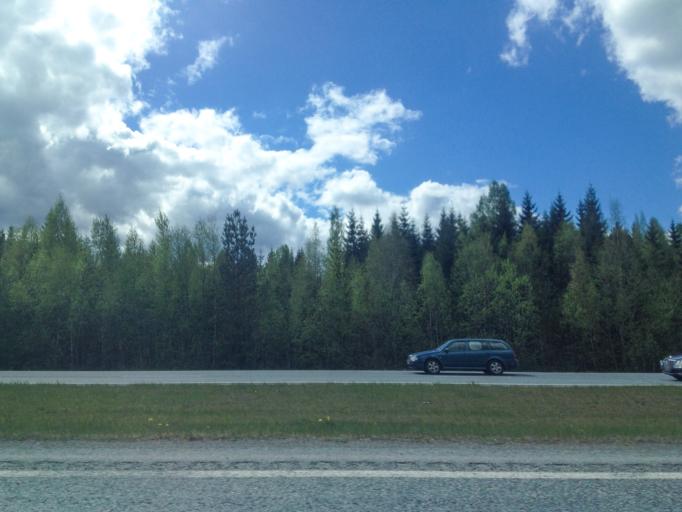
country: FI
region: Haeme
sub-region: Haemeenlinna
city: Janakkala
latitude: 60.9168
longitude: 24.5351
